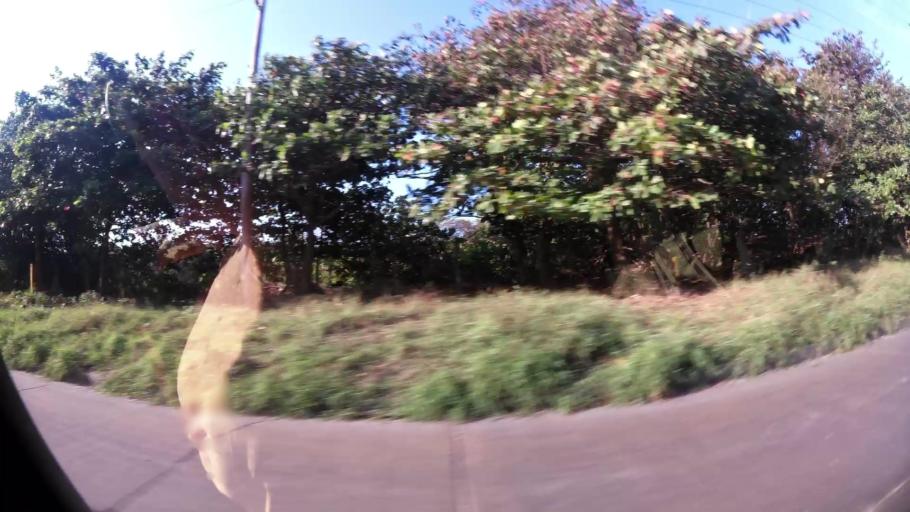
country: CO
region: Atlantico
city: Barranquilla
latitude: 11.0339
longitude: -74.8122
